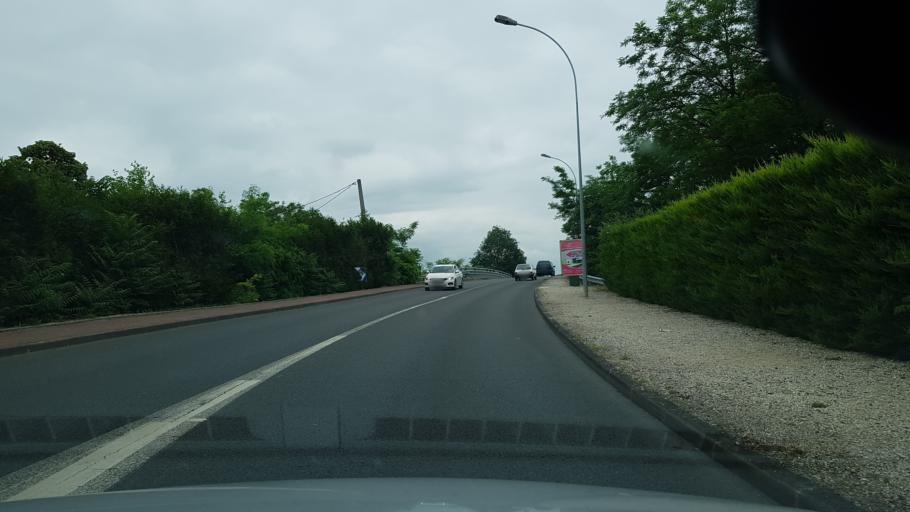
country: FR
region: Centre
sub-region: Departement du Loir-et-Cher
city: Selles-sur-Cher
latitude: 47.2830
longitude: 1.5425
